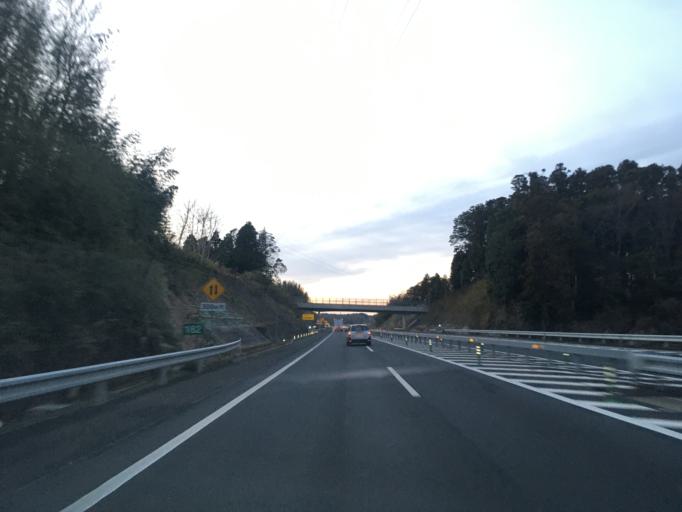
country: JP
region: Ibaraki
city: Edosaki
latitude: 35.9369
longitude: 140.3348
